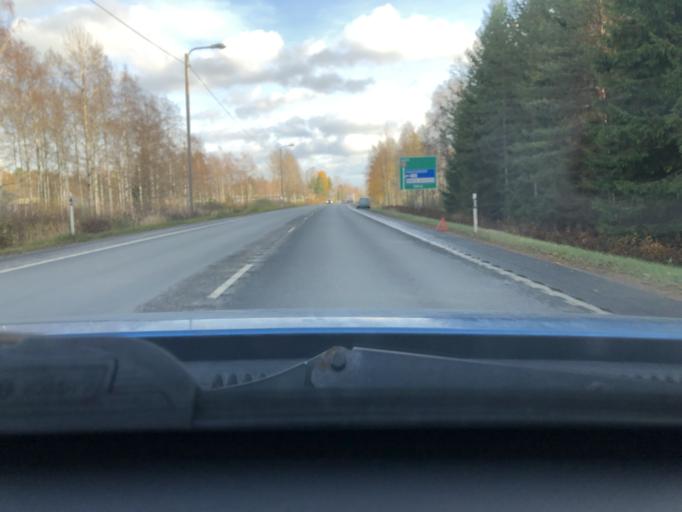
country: FI
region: Pirkanmaa
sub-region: Tampere
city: Kangasala
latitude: 61.4661
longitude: 24.0188
